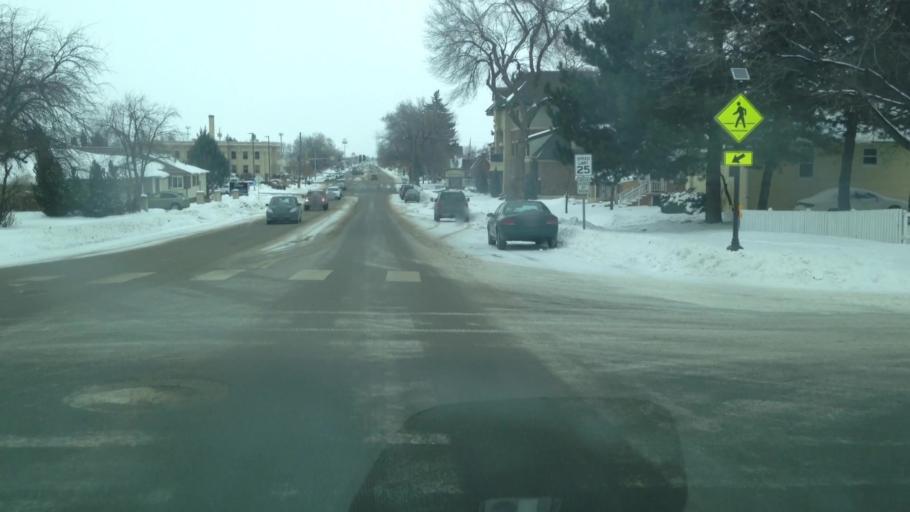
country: US
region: Idaho
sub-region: Madison County
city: Rexburg
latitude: 43.8239
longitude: -111.7781
